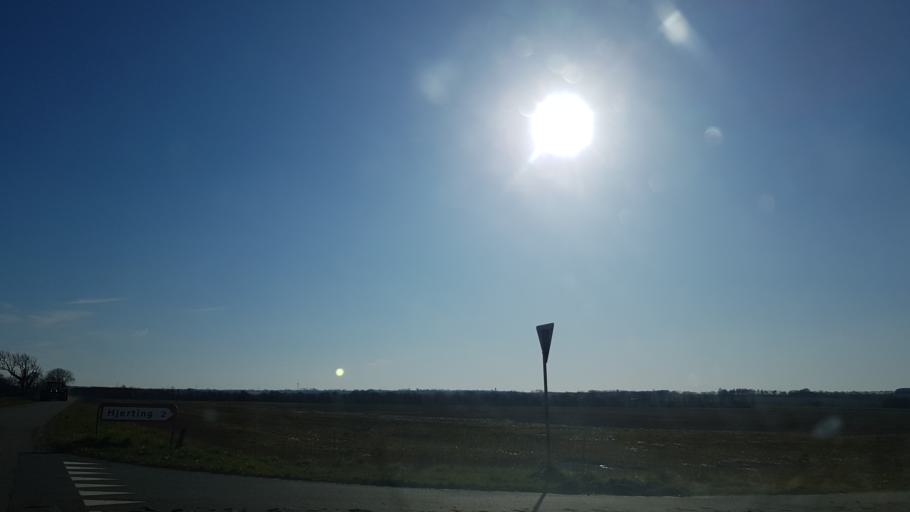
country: DK
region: South Denmark
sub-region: Vejen Kommune
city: Rodding
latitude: 55.3852
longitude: 9.0575
